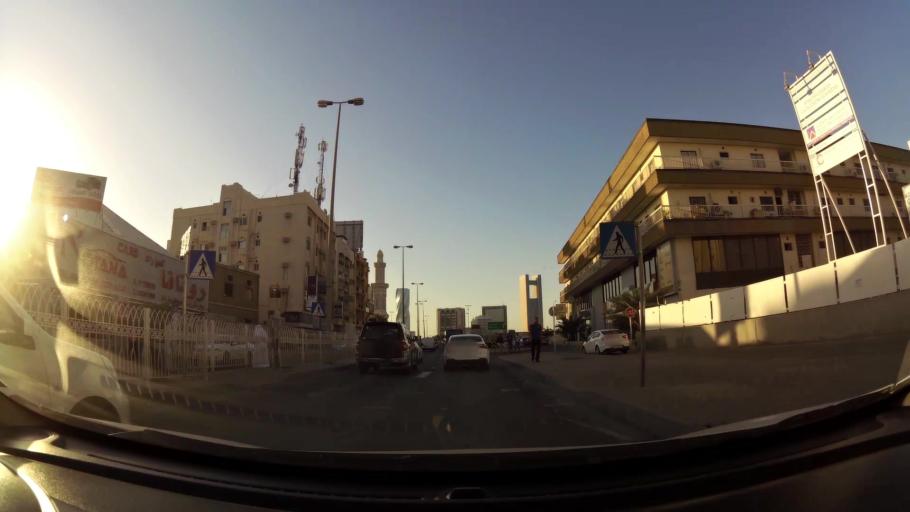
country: BH
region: Manama
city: Manama
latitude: 26.2359
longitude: 50.5876
